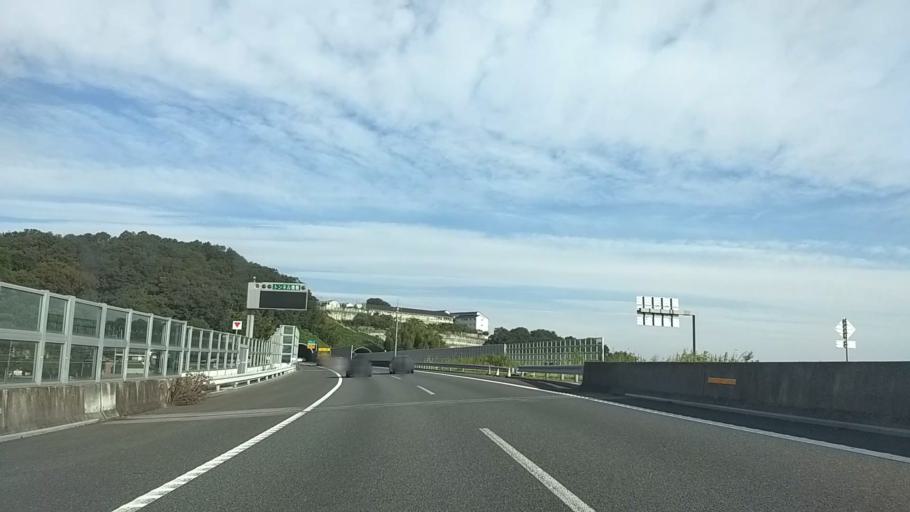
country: JP
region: Kanagawa
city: Zama
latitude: 35.5070
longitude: 139.3659
